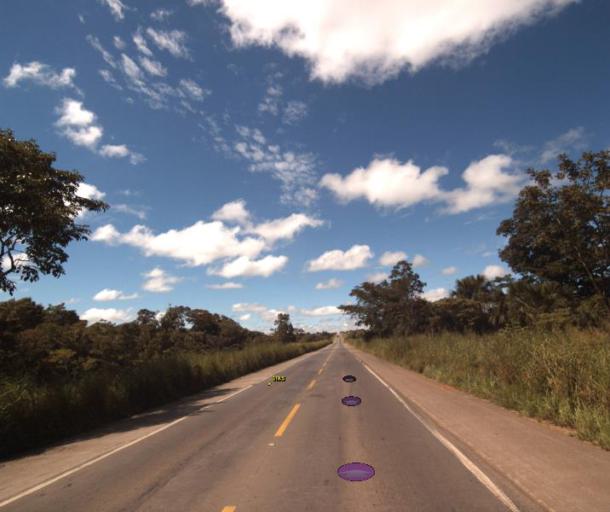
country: BR
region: Goias
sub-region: Rialma
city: Rialma
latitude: -15.4356
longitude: -49.5104
